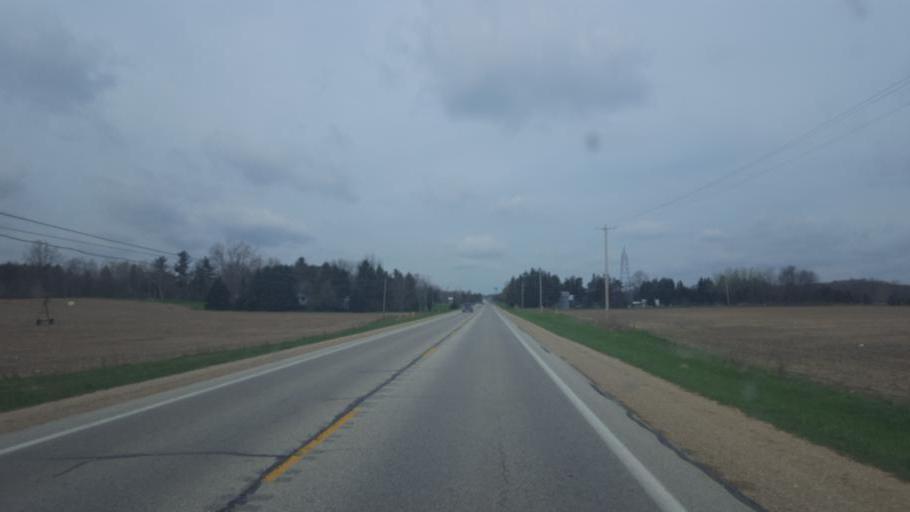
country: US
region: Michigan
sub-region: Montcalm County
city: Edmore
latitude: 43.4081
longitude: -85.0110
